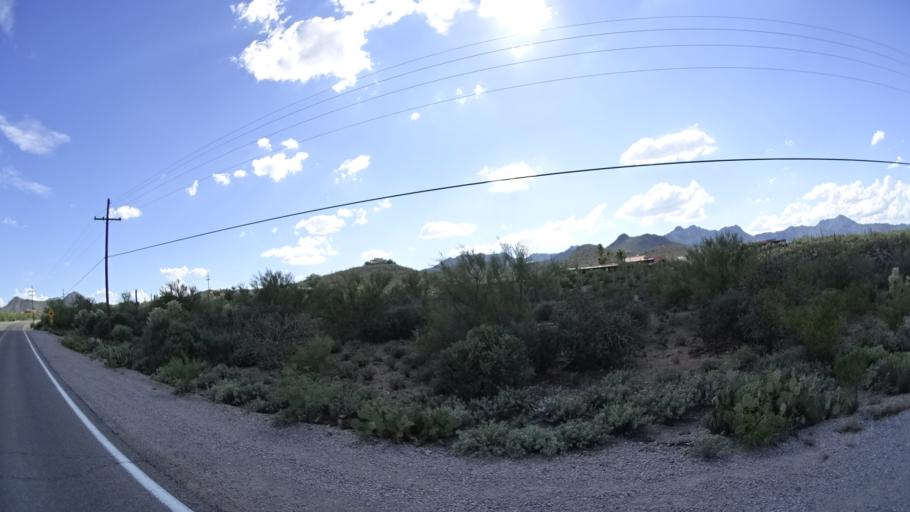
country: US
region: Arizona
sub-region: Pima County
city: Flowing Wells
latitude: 32.2579
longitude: -111.0619
